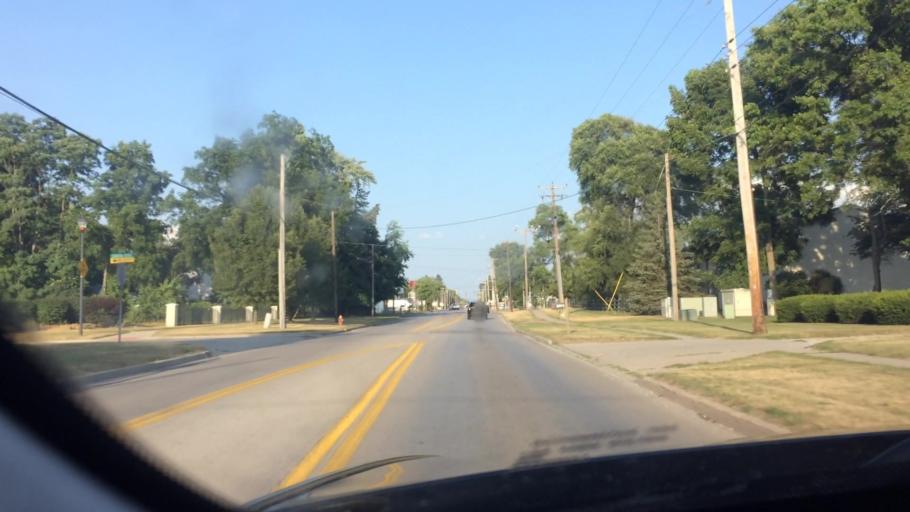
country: US
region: Ohio
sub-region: Lucas County
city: Holland
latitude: 41.6538
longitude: -83.6860
